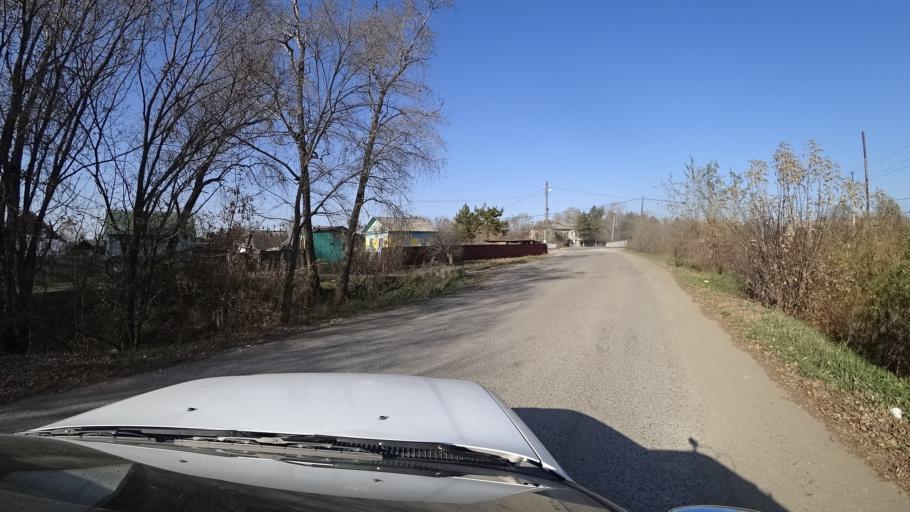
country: RU
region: Primorskiy
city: Dal'nerechensk
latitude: 45.9243
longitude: 133.7259
